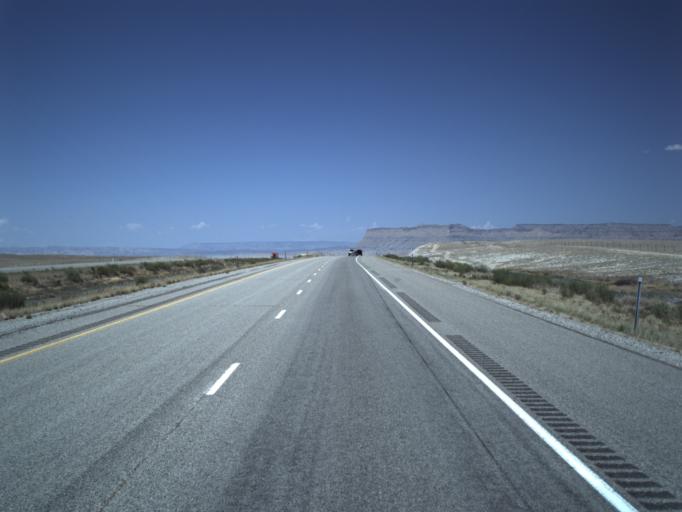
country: US
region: Utah
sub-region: Grand County
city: Moab
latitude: 38.9521
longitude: -110.0499
